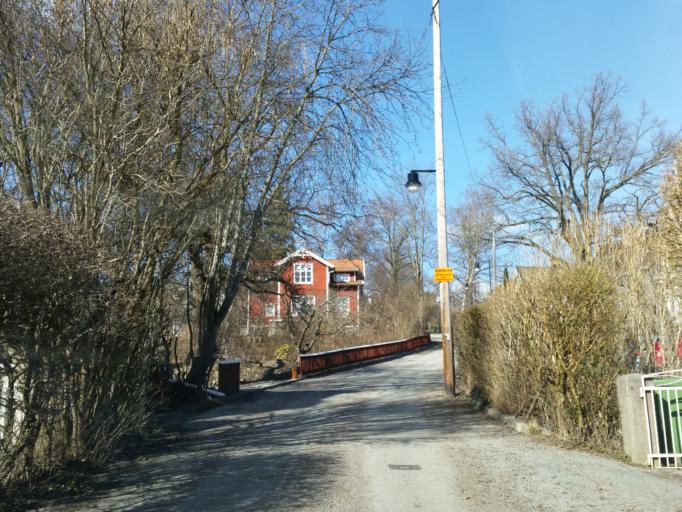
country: SE
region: Stockholm
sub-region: Sundbybergs Kommun
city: Sundbyberg
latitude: 59.3711
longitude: 17.9595
